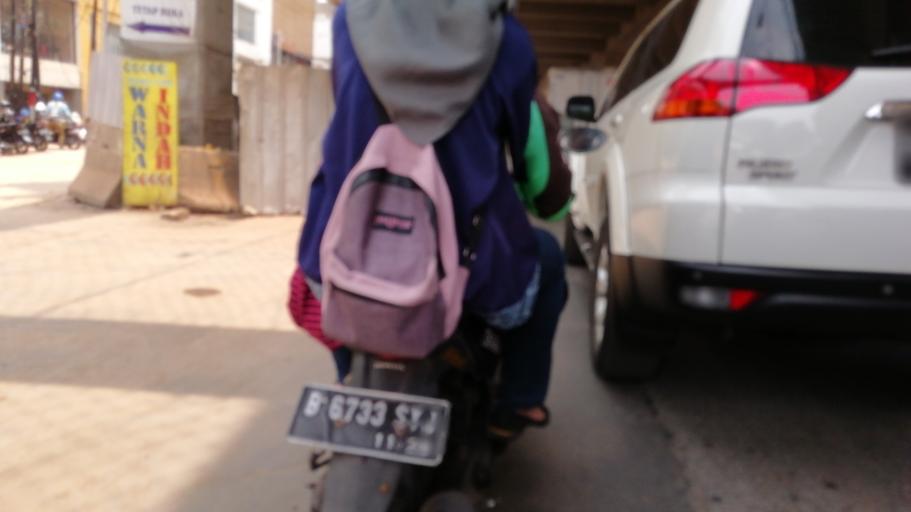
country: ID
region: Jakarta Raya
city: Jakarta
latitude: -6.2675
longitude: 106.7972
